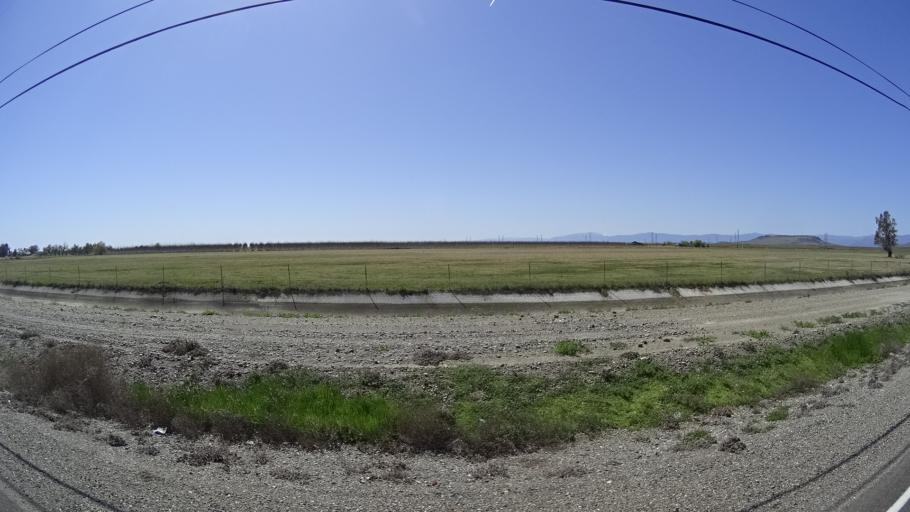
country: US
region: California
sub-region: Glenn County
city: Orland
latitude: 39.7692
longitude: -122.2544
